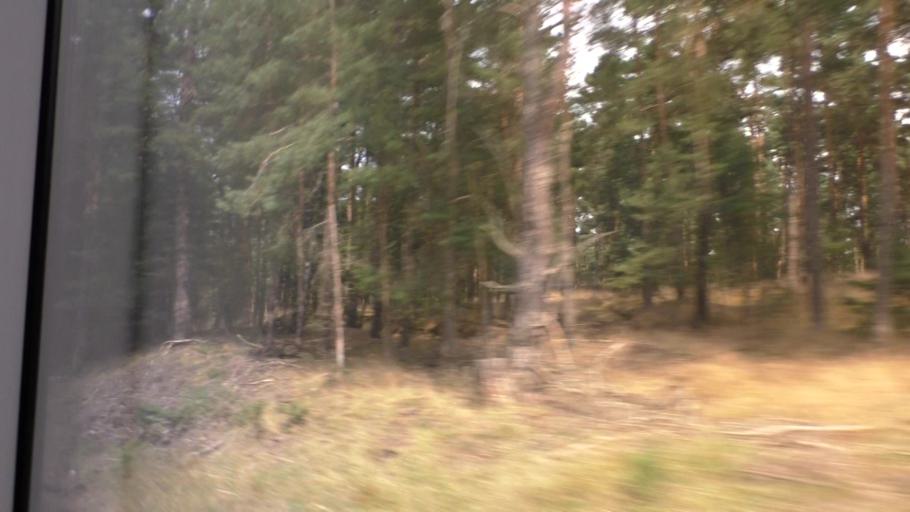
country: DE
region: Brandenburg
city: Mixdorf
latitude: 52.1748
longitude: 14.3819
